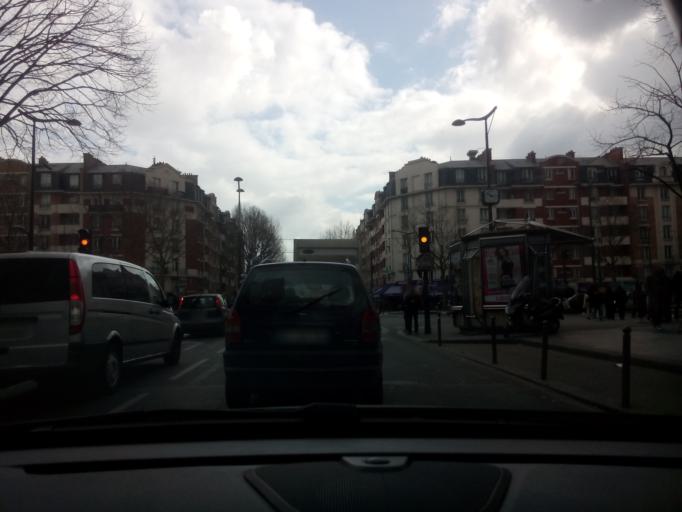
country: FR
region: Ile-de-France
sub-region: Departement du Val-de-Marne
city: Le Kremlin-Bicetre
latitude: 48.8205
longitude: 2.3644
